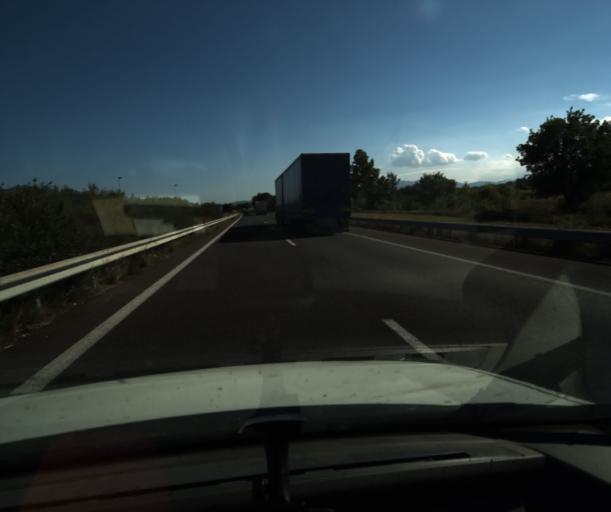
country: FR
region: Languedoc-Roussillon
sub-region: Departement des Pyrenees-Orientales
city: Villemolaque
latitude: 42.5754
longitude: 2.8441
